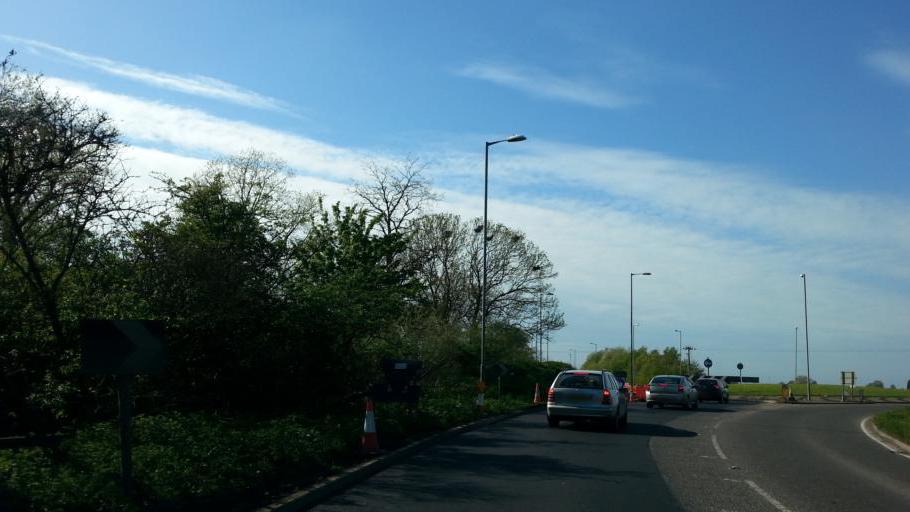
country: GB
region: England
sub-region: Cambridgeshire
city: Chatteris
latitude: 52.4292
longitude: 0.0884
